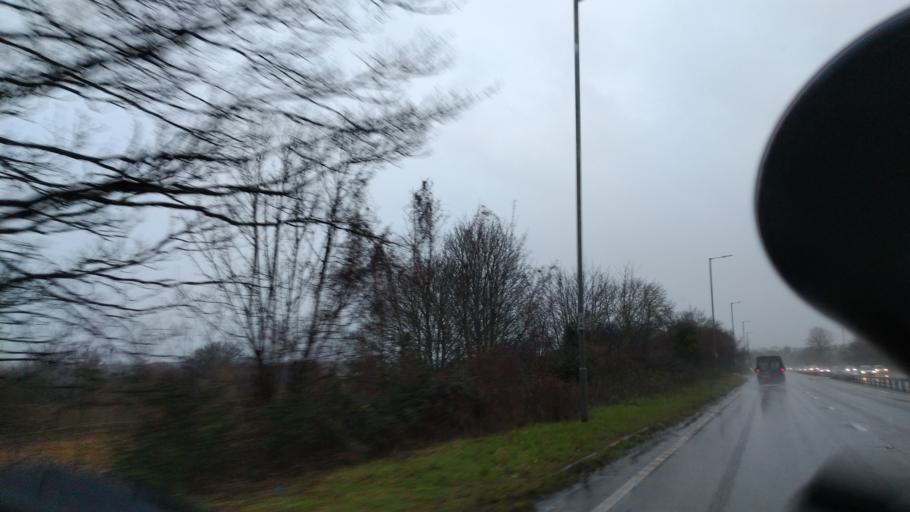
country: GB
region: England
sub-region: West Sussex
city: Broadwater
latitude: 50.8366
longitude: -0.3521
